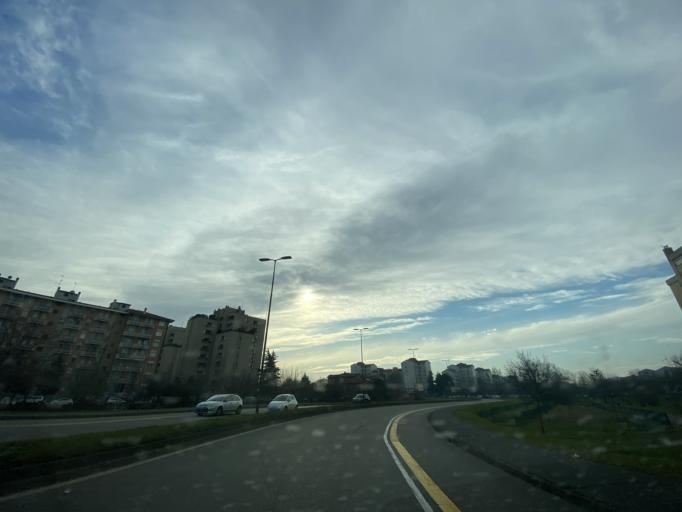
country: IT
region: Lombardy
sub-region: Citta metropolitana di Milano
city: Romano Banco
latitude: 45.4584
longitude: 9.1162
